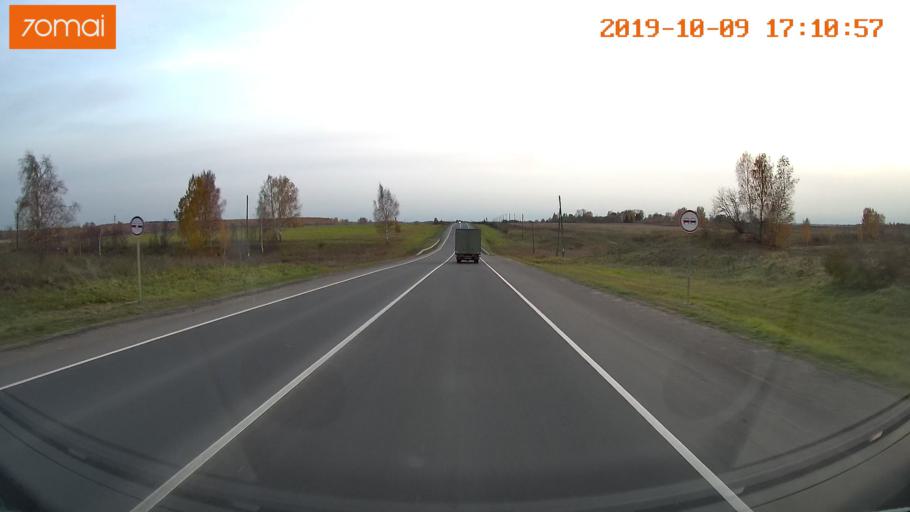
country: RU
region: Ivanovo
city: Privolzhsk
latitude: 57.3488
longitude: 41.2534
